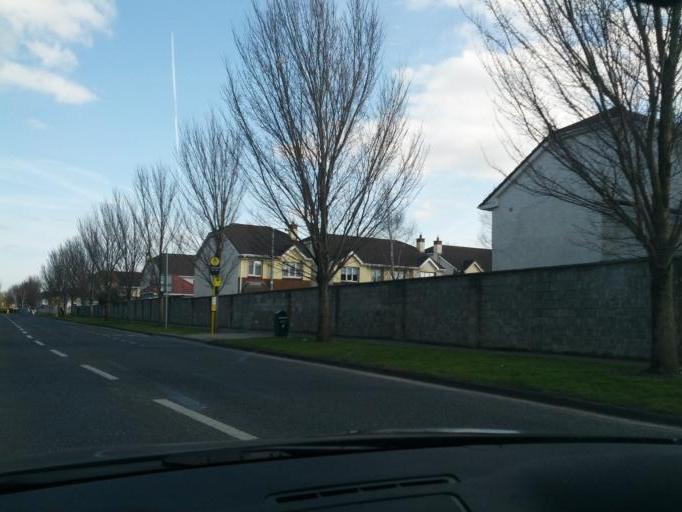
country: IE
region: Leinster
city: Lucan
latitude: 53.3401
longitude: -6.4278
